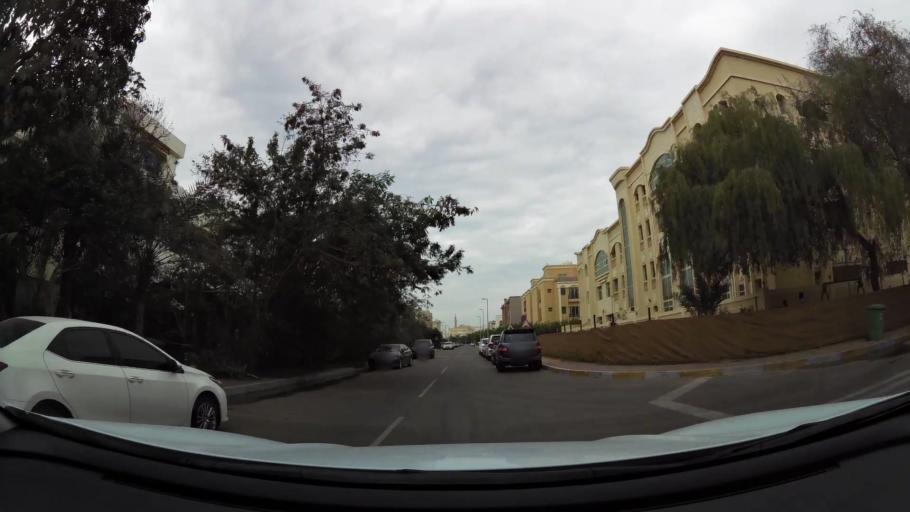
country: AE
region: Abu Dhabi
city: Abu Dhabi
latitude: 24.4376
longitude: 54.4098
